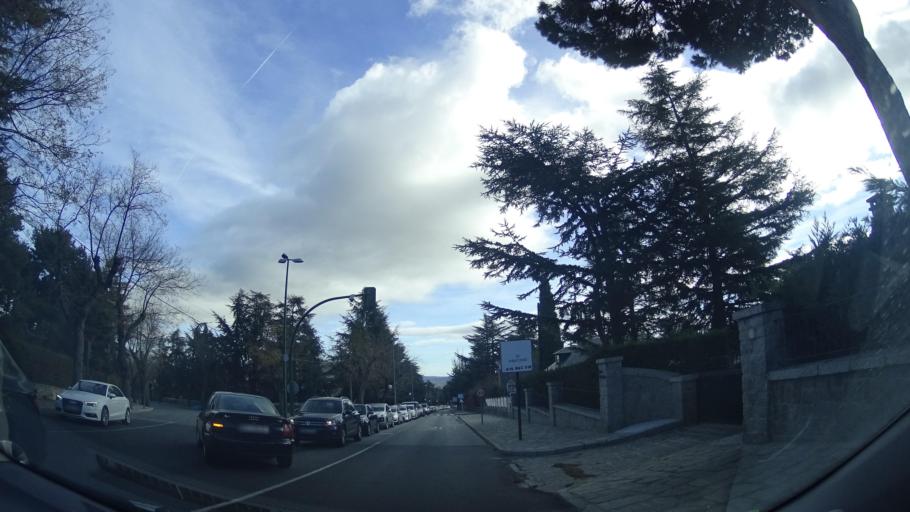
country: ES
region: Madrid
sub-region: Provincia de Madrid
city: San Lorenzo de El Escorial
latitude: 40.5891
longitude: -4.1381
